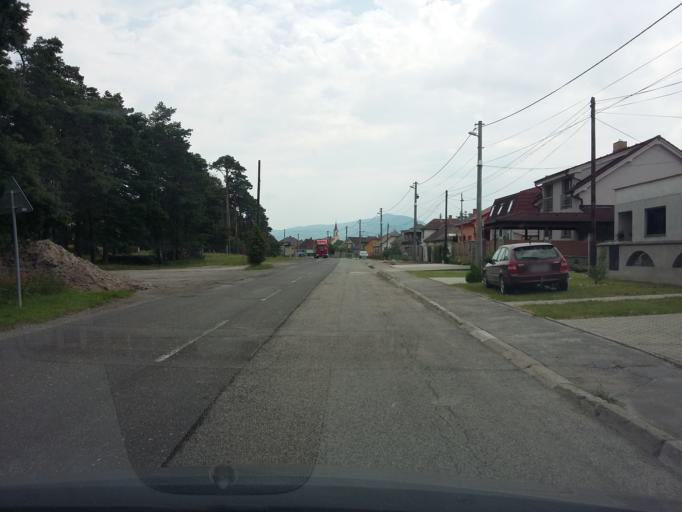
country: SK
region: Bratislavsky
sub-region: Okres Malacky
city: Malacky
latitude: 48.4612
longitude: 17.1567
